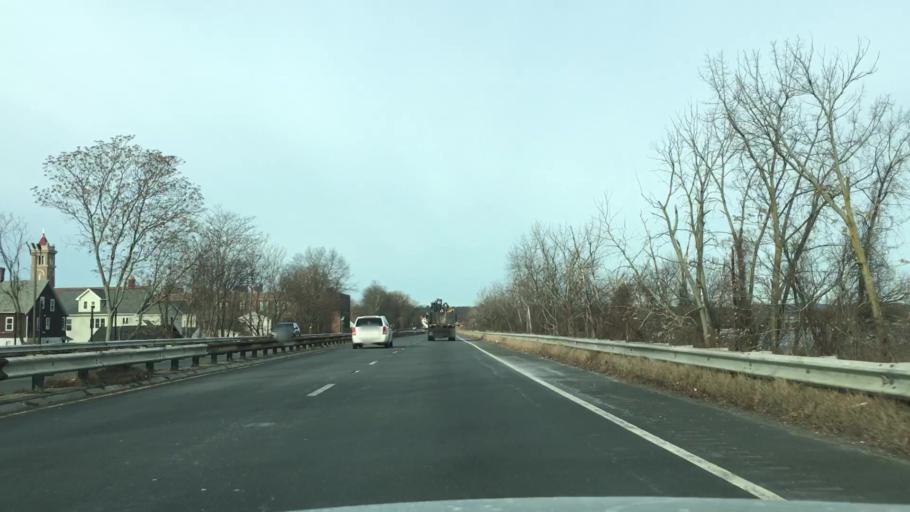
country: US
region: Massachusetts
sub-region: Hampden County
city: West Springfield
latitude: 42.1023
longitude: -72.6062
